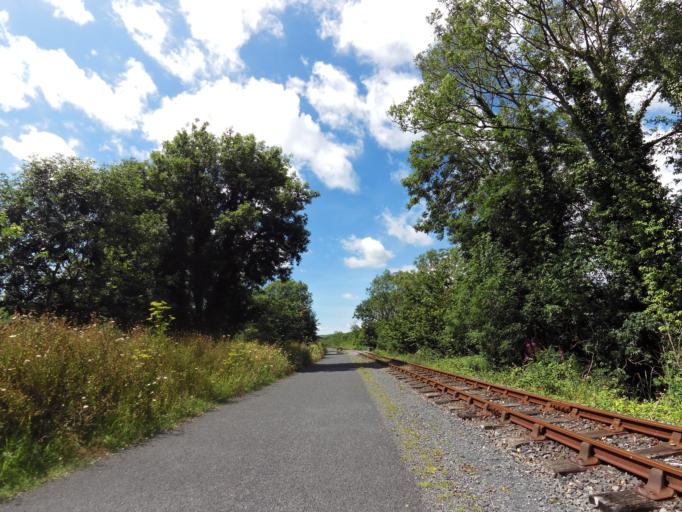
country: IE
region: Leinster
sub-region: Kilkenny
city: Mooncoin
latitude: 52.2469
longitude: -7.2341
